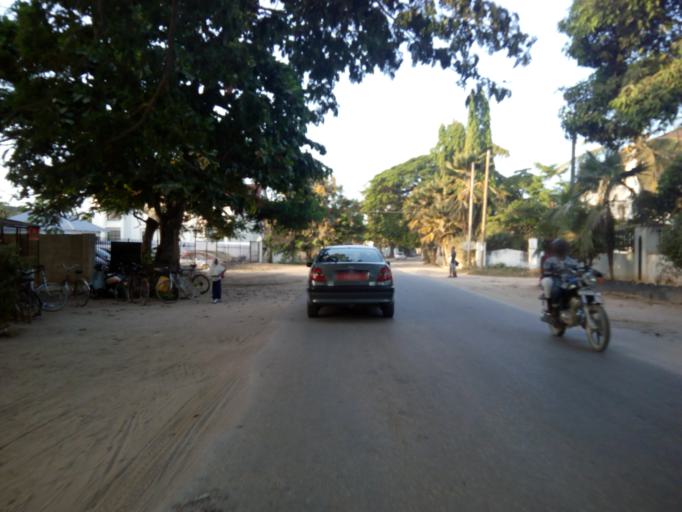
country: TZ
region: Zanzibar Urban/West
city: Zanzibar
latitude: -6.2054
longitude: 39.2100
